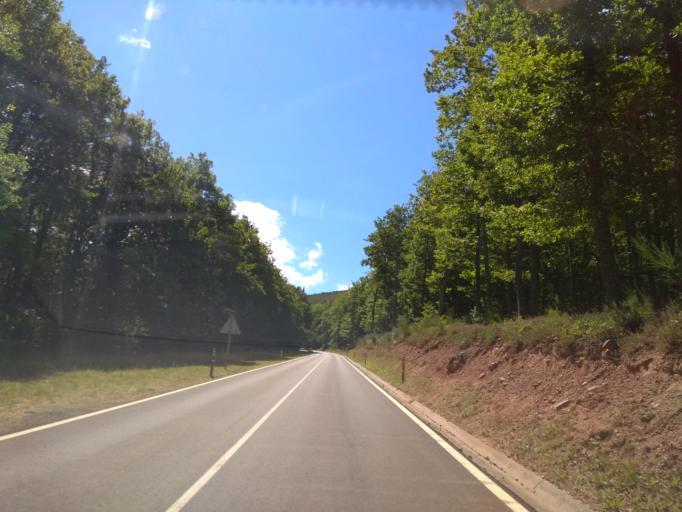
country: ES
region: Cantabria
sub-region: Provincia de Cantabria
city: Villaescusa
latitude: 42.9489
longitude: -4.1593
